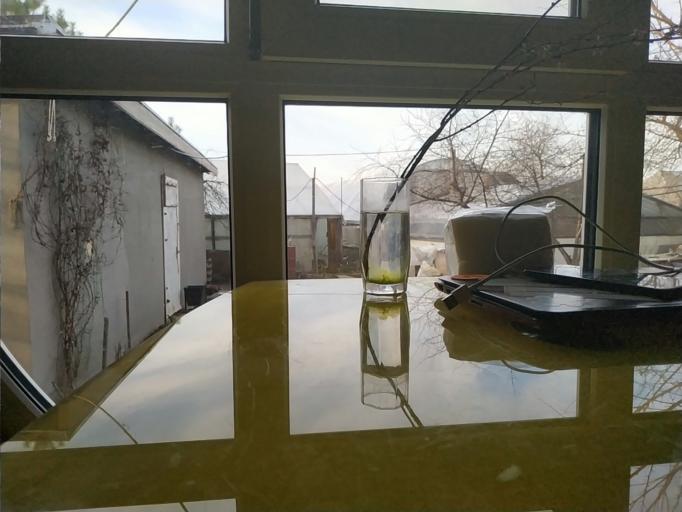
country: RU
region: Republic of Karelia
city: Suoyarvi
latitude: 61.9482
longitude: 32.2333
